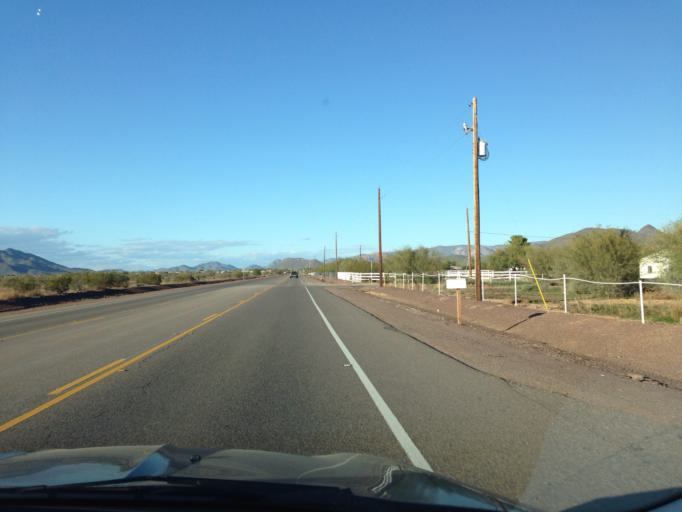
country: US
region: Arizona
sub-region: Maricopa County
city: Anthem
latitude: 33.8176
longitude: -112.0654
